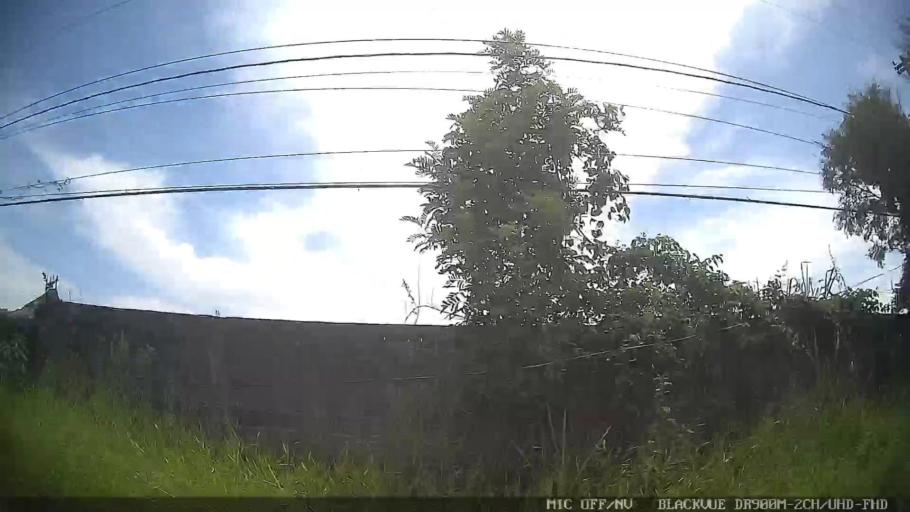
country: BR
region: Sao Paulo
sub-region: Santa Isabel
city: Santa Isabel
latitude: -23.3854
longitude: -46.1745
